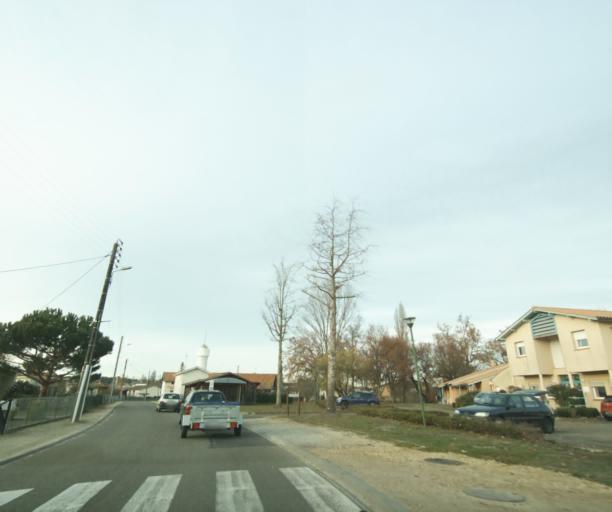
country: FR
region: Aquitaine
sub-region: Departement de la Gironde
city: Prechac
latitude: 44.2899
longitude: -0.2580
